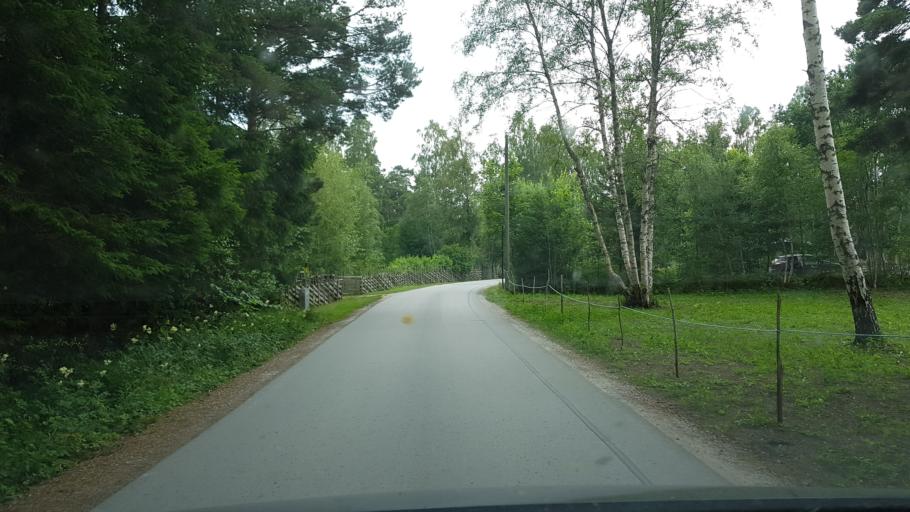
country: SE
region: Gotland
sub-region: Gotland
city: Hemse
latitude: 57.3379
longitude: 18.7081
